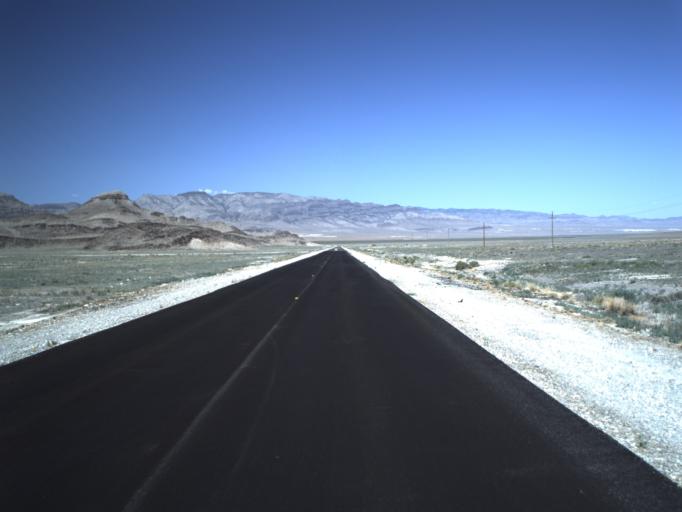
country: US
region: Utah
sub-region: Beaver County
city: Milford
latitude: 39.0506
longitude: -113.4196
